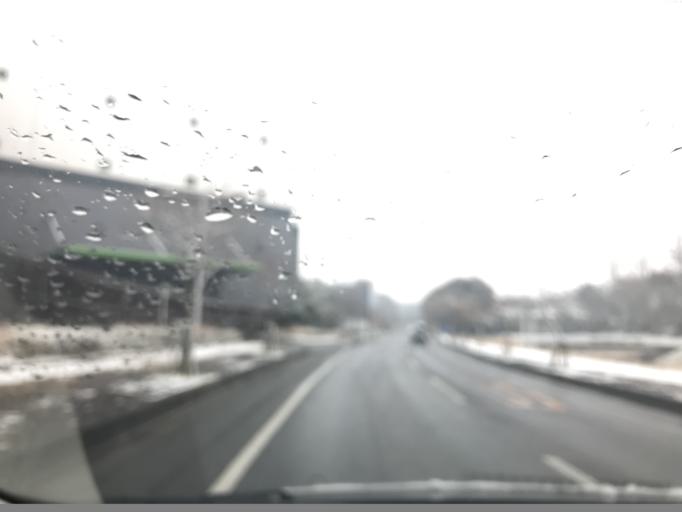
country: JP
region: Ibaraki
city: Moriya
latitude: 35.9568
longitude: 139.9587
